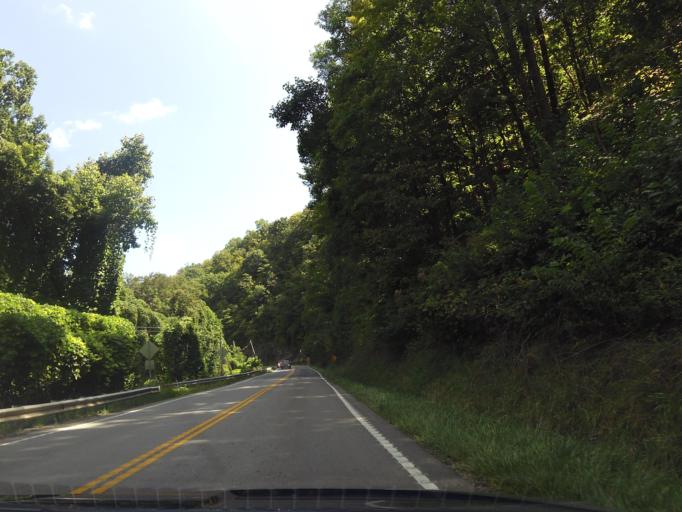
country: US
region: Kentucky
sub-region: Harlan County
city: Loyall
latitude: 36.8993
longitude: -83.3355
